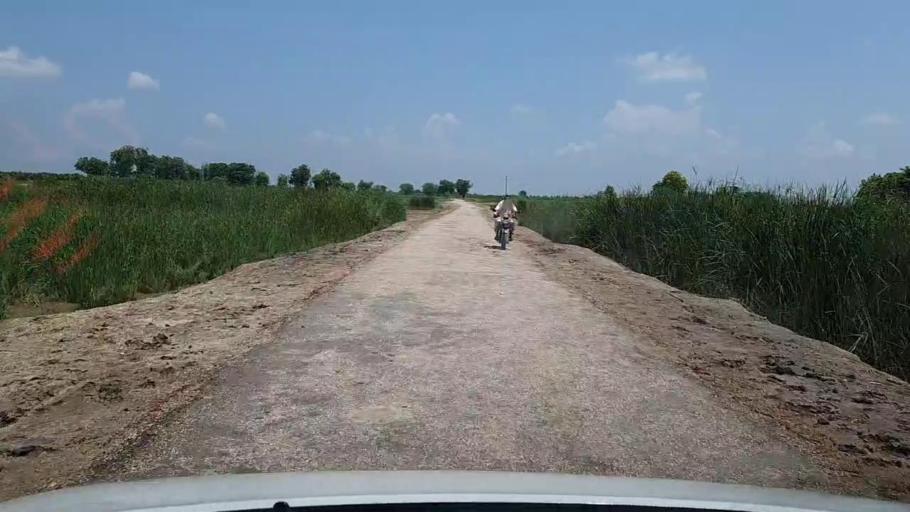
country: PK
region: Sindh
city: Bhiria
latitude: 26.9761
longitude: 68.2081
